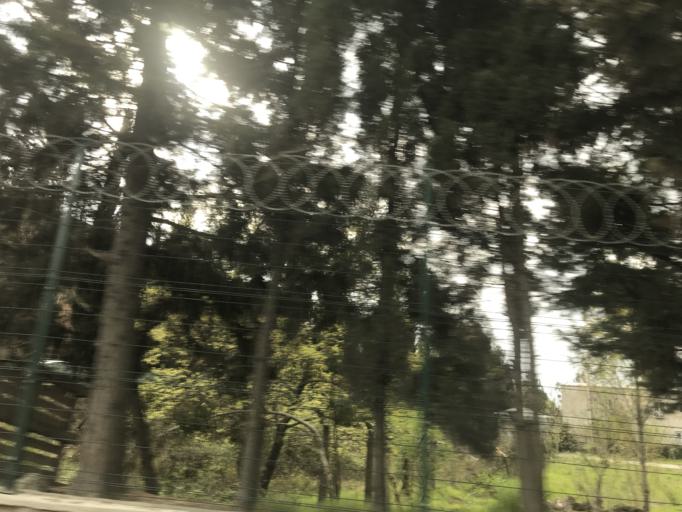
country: TR
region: Istanbul
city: Samandira
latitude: 40.9982
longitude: 29.1790
